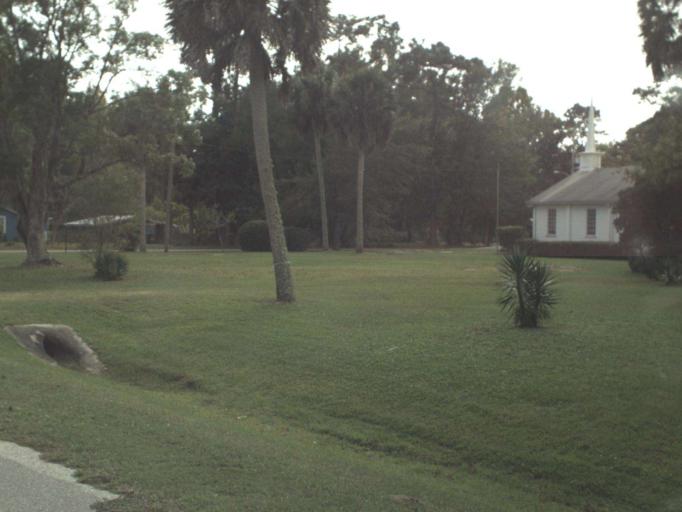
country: US
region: Florida
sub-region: Leon County
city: Woodville
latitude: 30.1617
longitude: -84.2064
